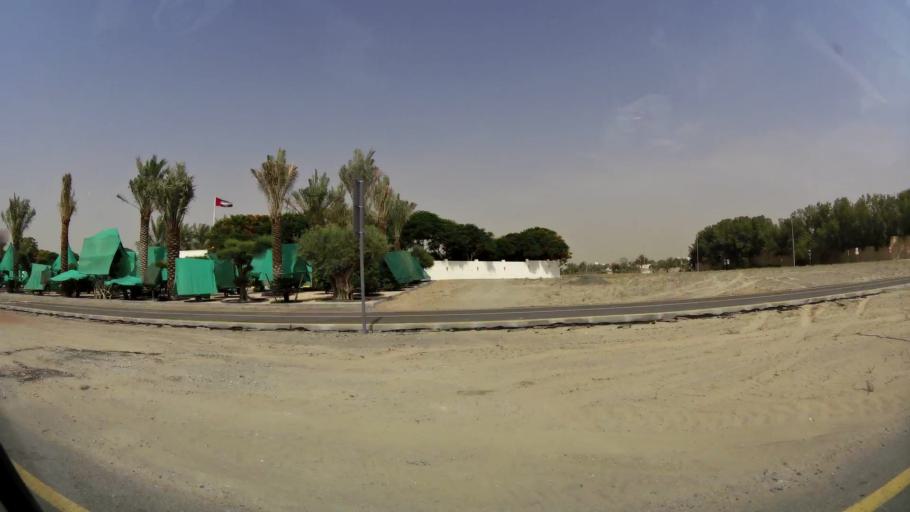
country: AE
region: Ash Shariqah
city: Sharjah
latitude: 25.2445
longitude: 55.4783
